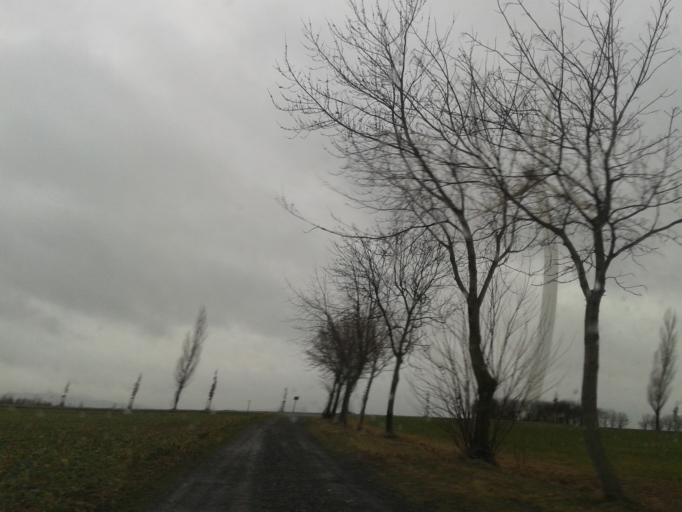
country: DE
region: Saxony
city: Neugersdorf
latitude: 50.9635
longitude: 14.6264
